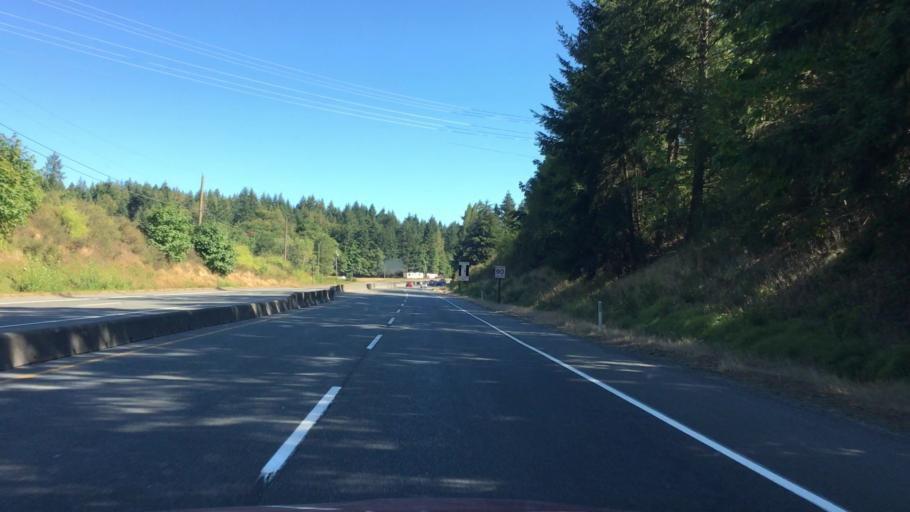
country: CA
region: British Columbia
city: North Cowichan
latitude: 48.8481
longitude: -123.7221
